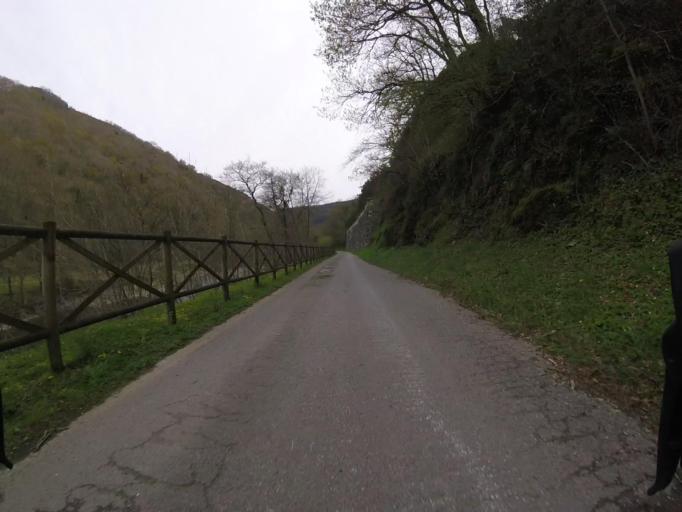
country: ES
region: Navarre
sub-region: Provincia de Navarra
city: Bera
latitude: 43.3013
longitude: -1.7333
